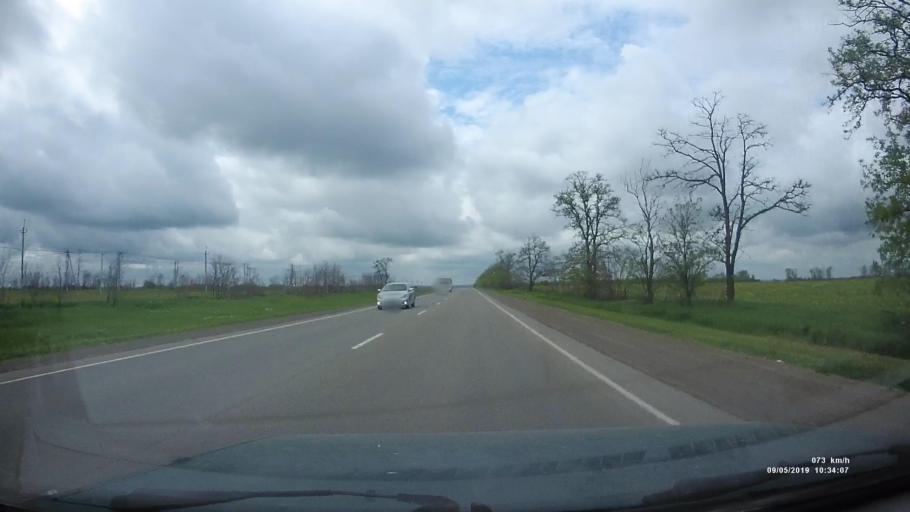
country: RU
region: Rostov
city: Azov
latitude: 47.0576
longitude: 39.4219
